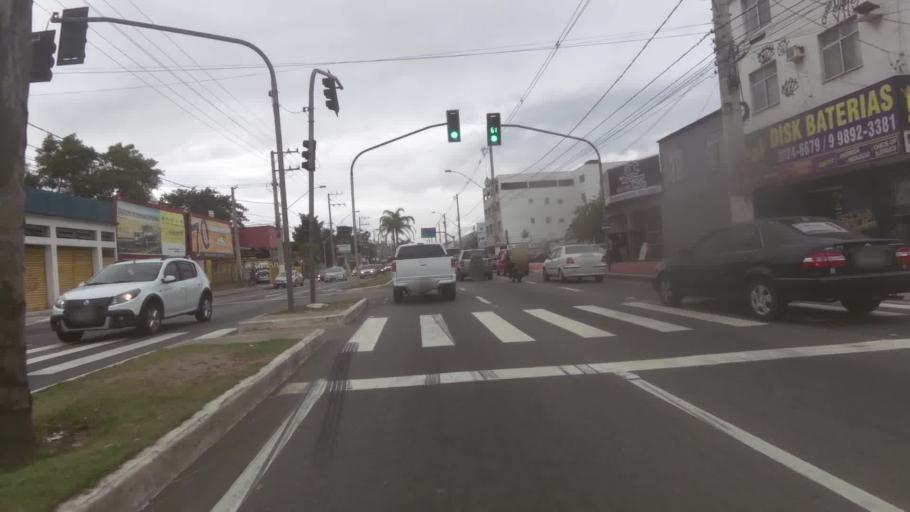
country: BR
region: Espirito Santo
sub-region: Vila Velha
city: Vila Velha
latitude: -20.2697
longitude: -40.3006
